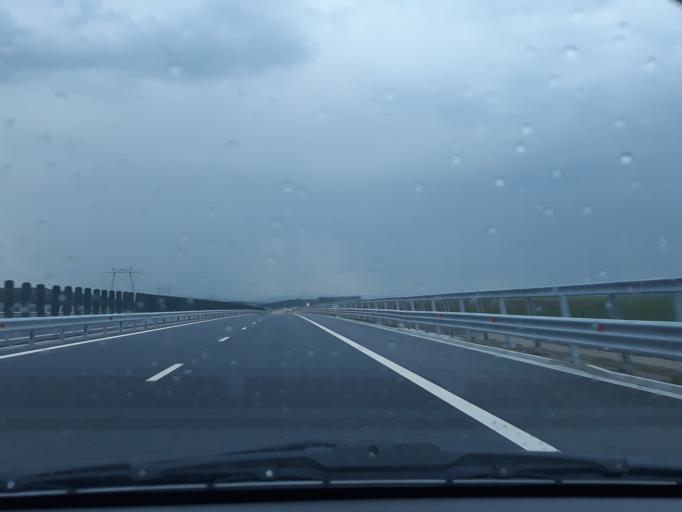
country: RO
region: Mures
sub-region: Comuna Sanpaul
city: Valea Izvoarelor
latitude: 46.4477
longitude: 24.3680
